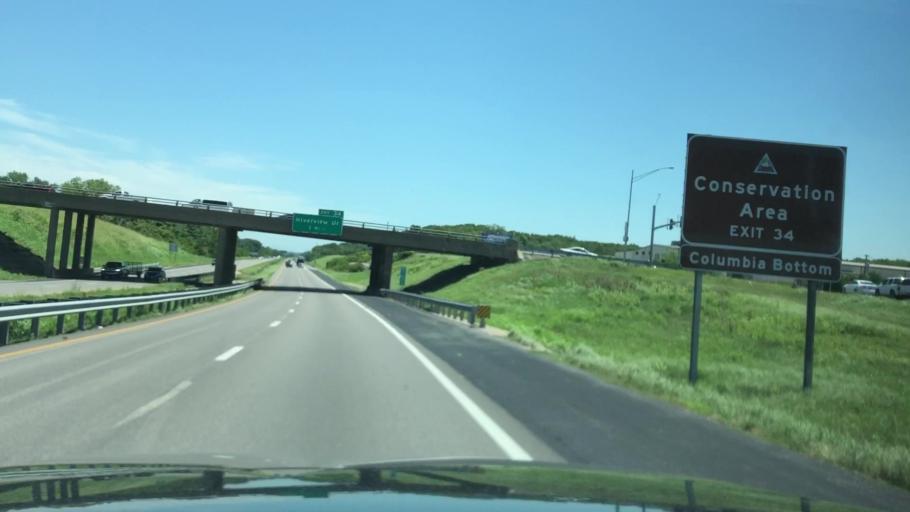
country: US
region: Missouri
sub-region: Saint Louis County
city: Glasgow Village
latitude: 38.7672
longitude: -90.2040
